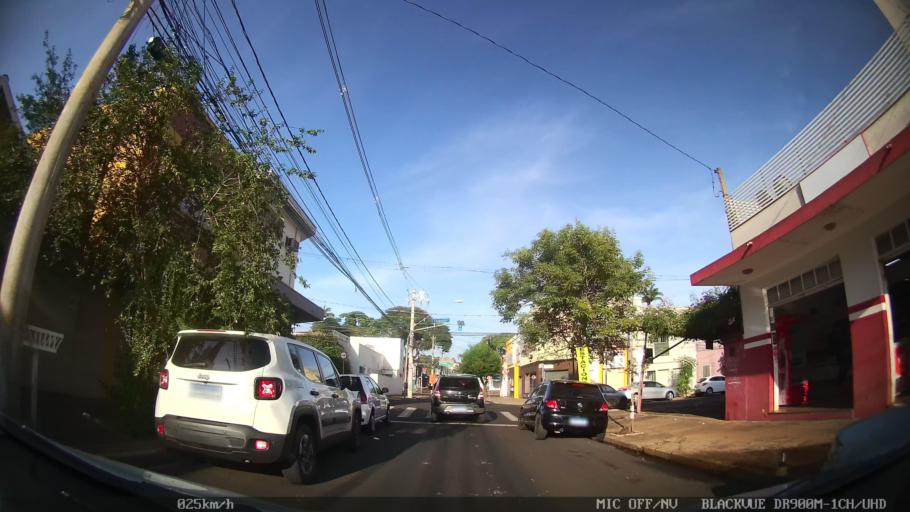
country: BR
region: Sao Paulo
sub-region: Ribeirao Preto
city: Ribeirao Preto
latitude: -21.1868
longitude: -47.8073
